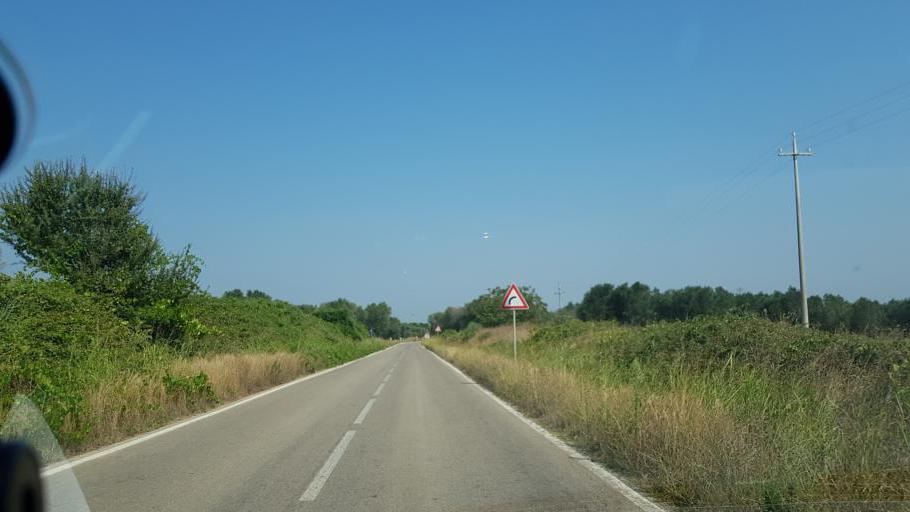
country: IT
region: Apulia
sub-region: Provincia di Brindisi
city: Torre Santa Susanna
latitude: 40.4989
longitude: 17.7294
